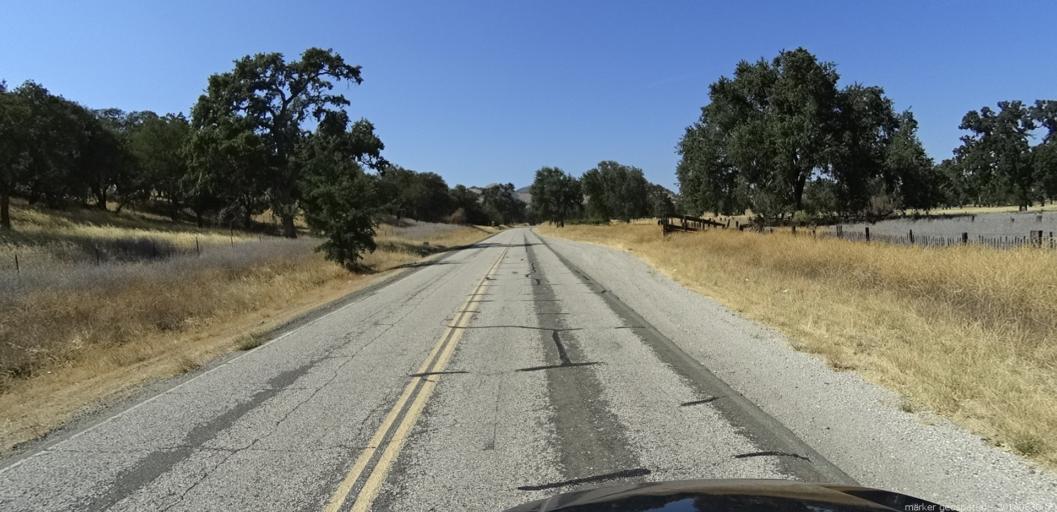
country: US
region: California
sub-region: Monterey County
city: King City
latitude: 36.0361
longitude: -121.1795
